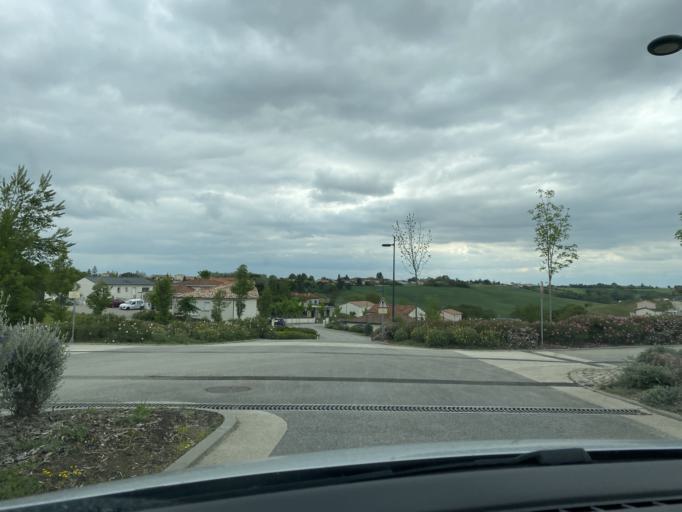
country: FR
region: Midi-Pyrenees
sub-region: Departement de la Haute-Garonne
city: Nailloux
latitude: 43.3617
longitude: 1.6236
